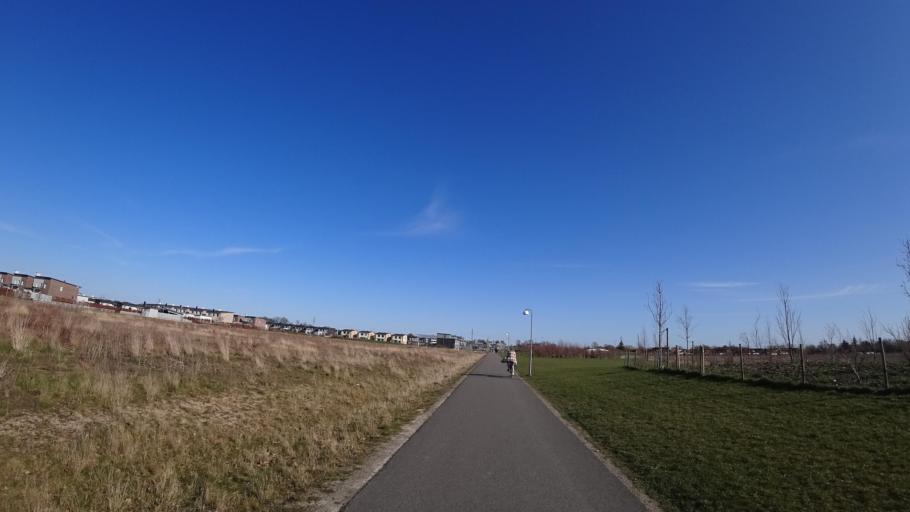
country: SE
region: Skane
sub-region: Staffanstorps Kommun
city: Hjaerup
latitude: 55.6710
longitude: 13.1483
